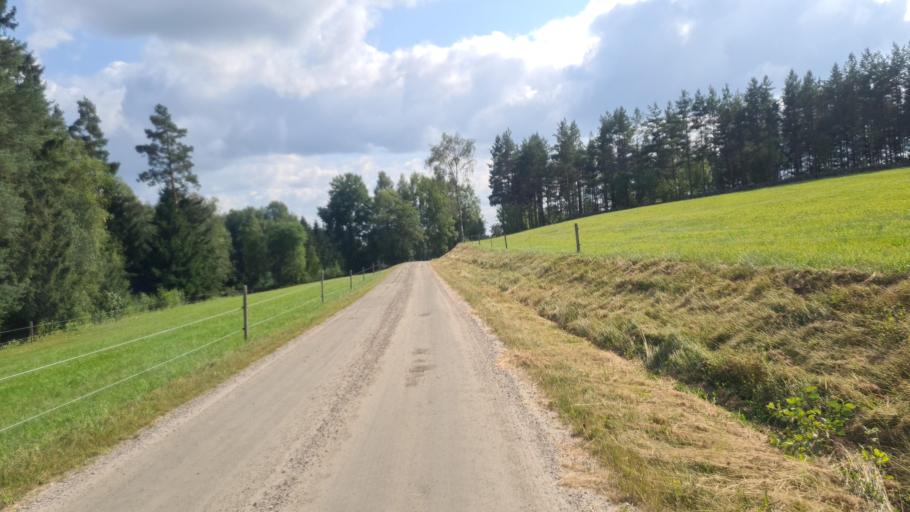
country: SE
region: Kronoberg
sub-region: Ljungby Kommun
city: Ljungby
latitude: 56.7207
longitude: 13.8813
